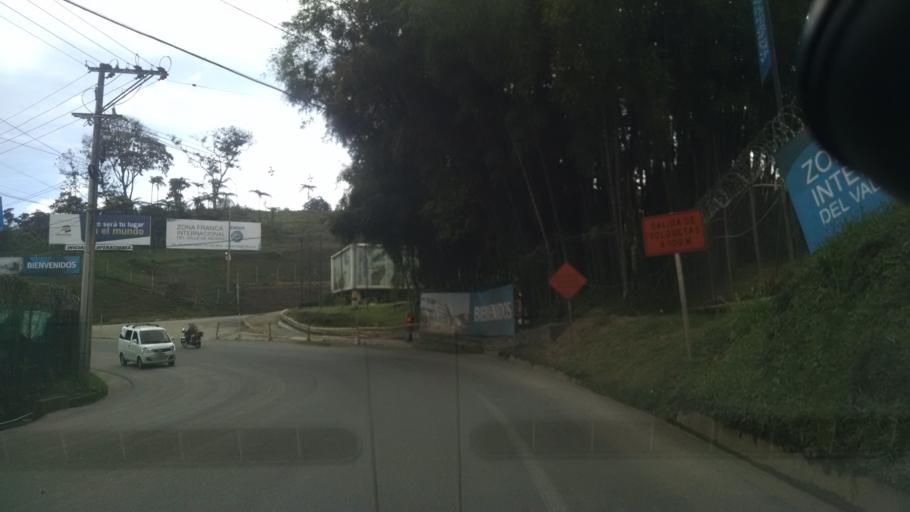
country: CO
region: Antioquia
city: Caldas
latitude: 6.0672
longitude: -75.6335
